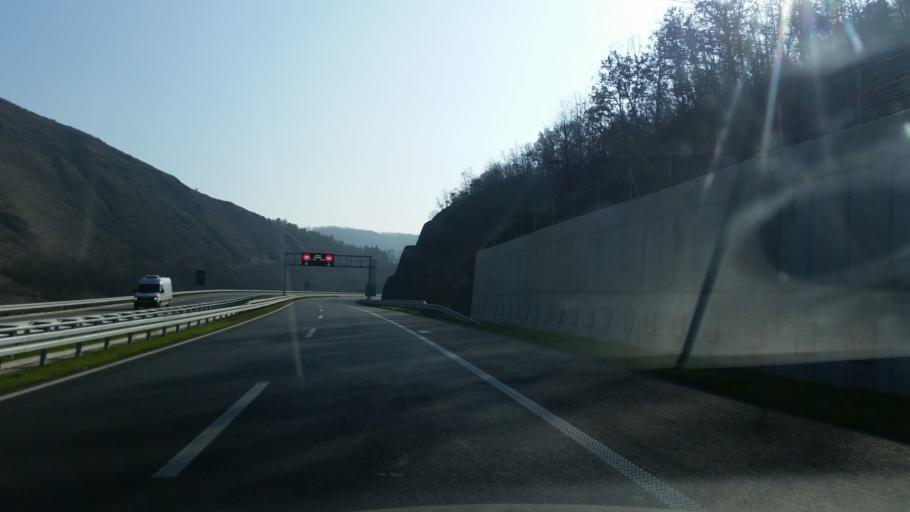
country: RS
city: Prislonica
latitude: 43.9888
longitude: 20.4000
